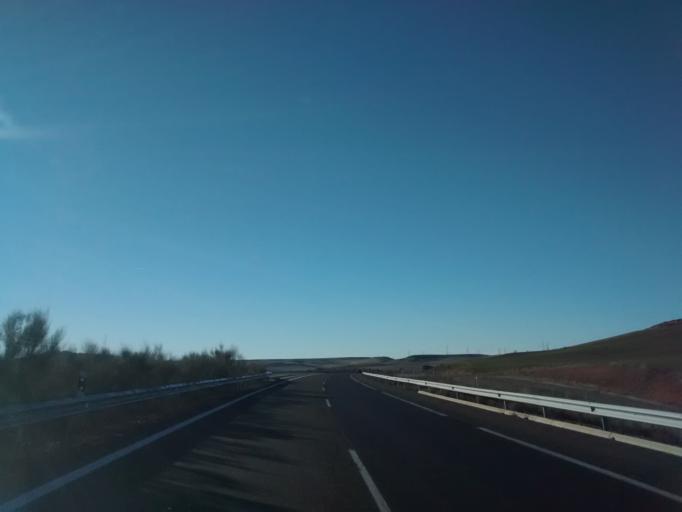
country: ES
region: Castille and Leon
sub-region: Provincia de Palencia
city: Herrera de Pisuerga
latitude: 42.5745
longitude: -4.3456
